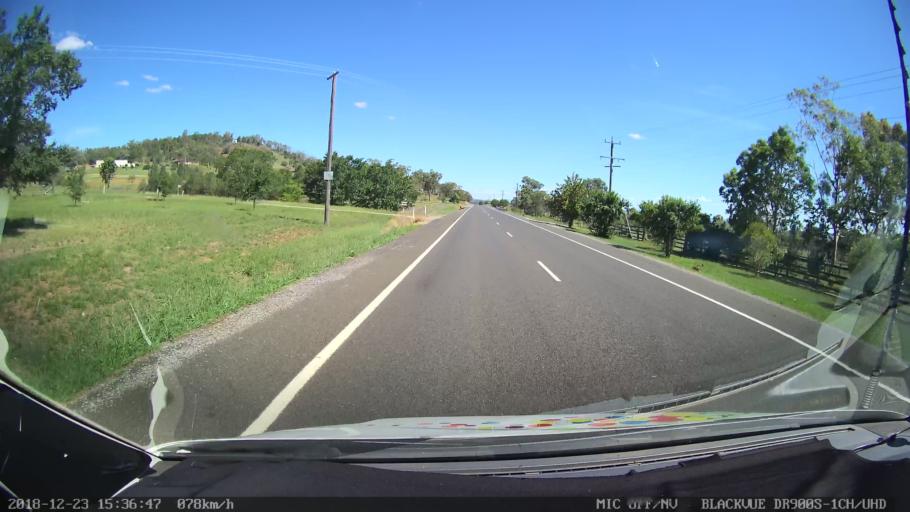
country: AU
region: New South Wales
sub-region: Tamworth Municipality
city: Tamworth
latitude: -31.0450
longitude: 150.8879
